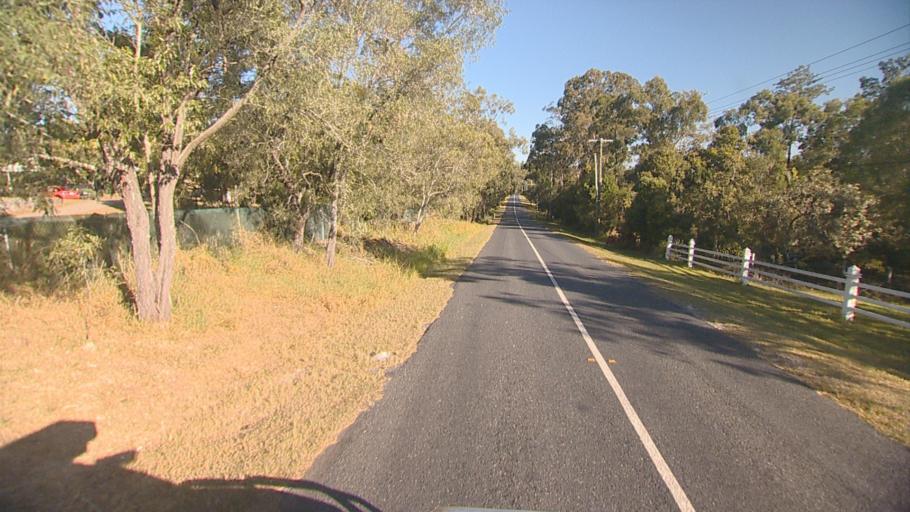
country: AU
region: Queensland
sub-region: Logan
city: Logan Reserve
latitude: -27.7317
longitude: 153.1043
